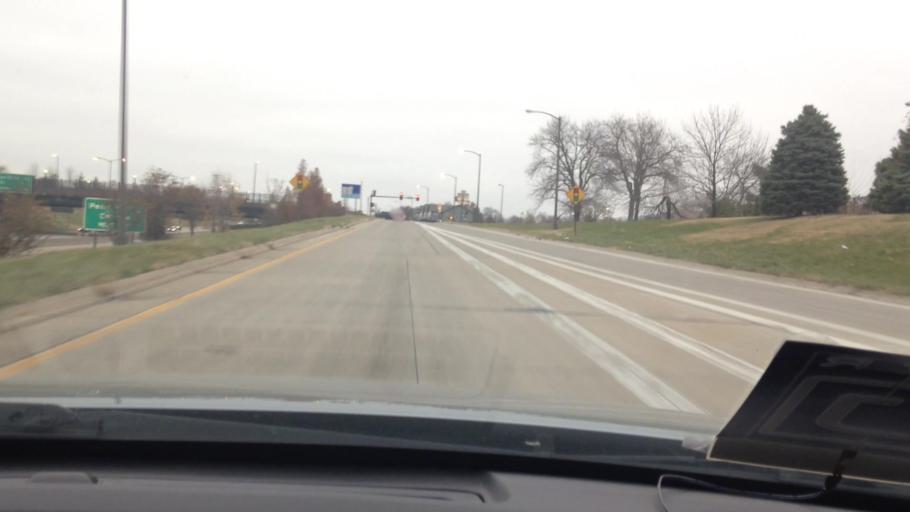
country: US
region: Missouri
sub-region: Jackson County
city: Kansas City
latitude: 39.0538
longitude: -94.5610
